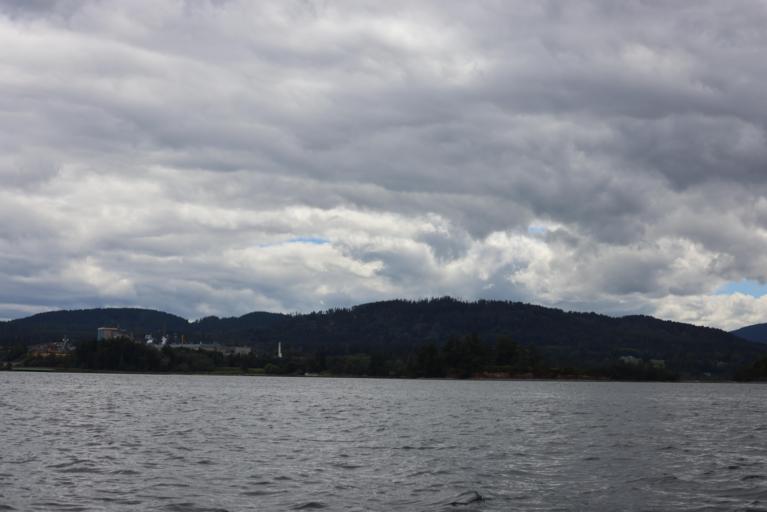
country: CA
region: British Columbia
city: North Cowichan
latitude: 48.8940
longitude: -123.6409
